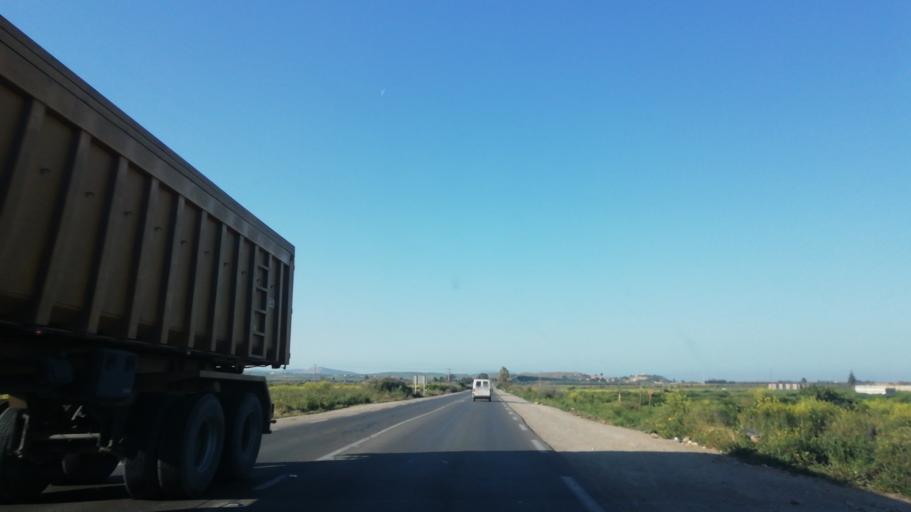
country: DZ
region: Mascara
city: Mascara
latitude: 35.6584
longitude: 0.1953
